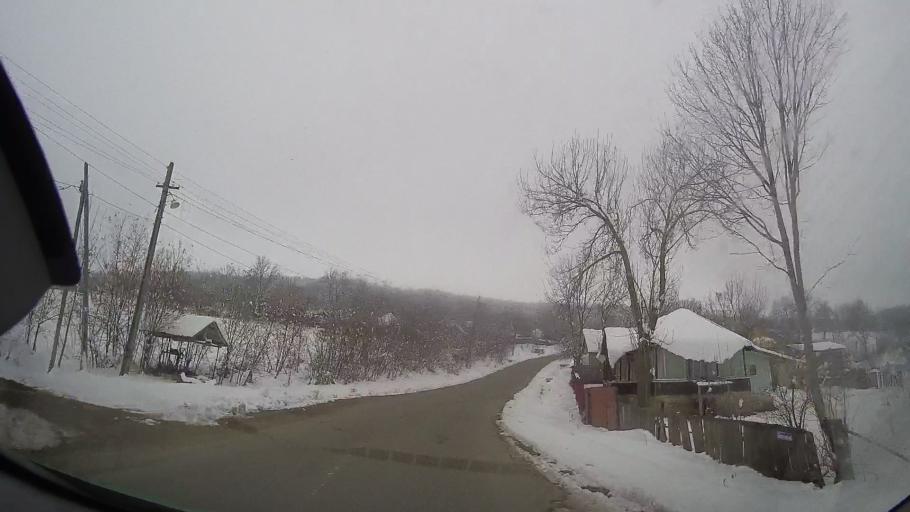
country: RO
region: Neamt
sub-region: Comuna Bozieni
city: Bozieni
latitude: 46.8522
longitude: 27.1798
